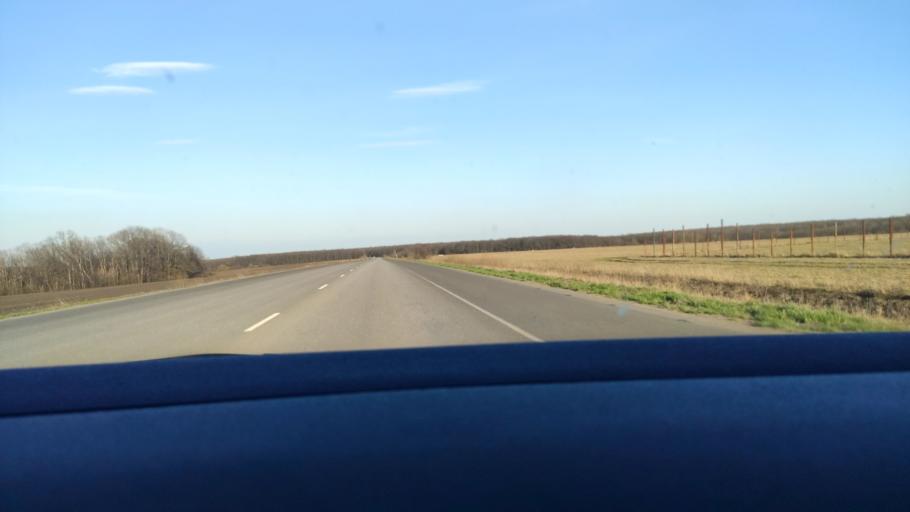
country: RU
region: Voronezj
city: Kolodeznyy
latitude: 51.3401
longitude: 39.0423
